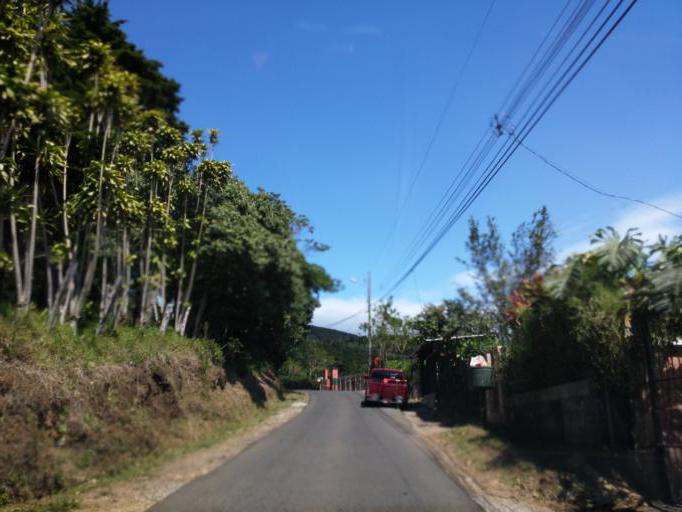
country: CR
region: Heredia
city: Santo Domingo
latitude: 10.0664
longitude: -84.1272
